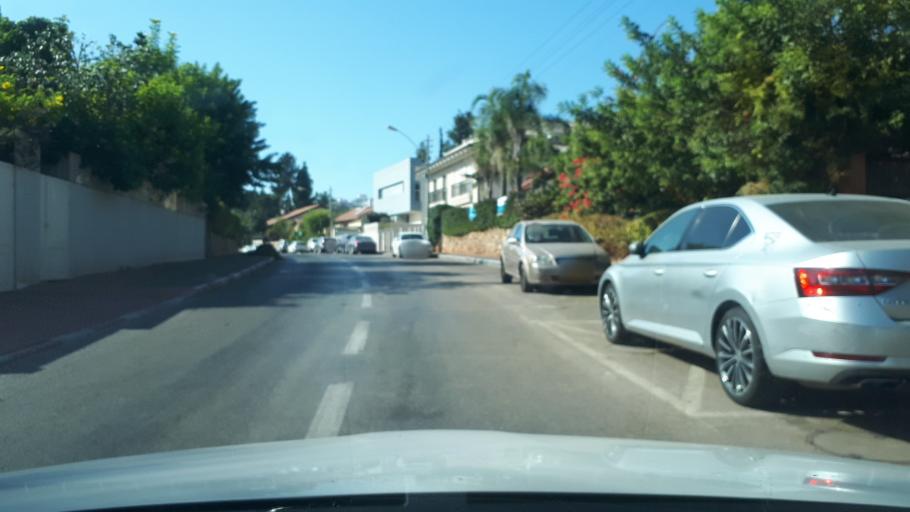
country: IL
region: Tel Aviv
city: Giv`atayim
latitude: 32.0586
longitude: 34.8246
